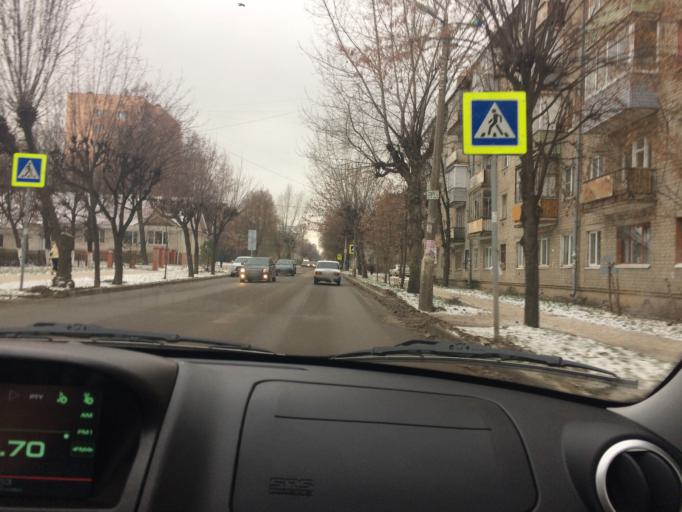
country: RU
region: Rjazan
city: Ryazan'
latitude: 54.6207
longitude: 39.7211
